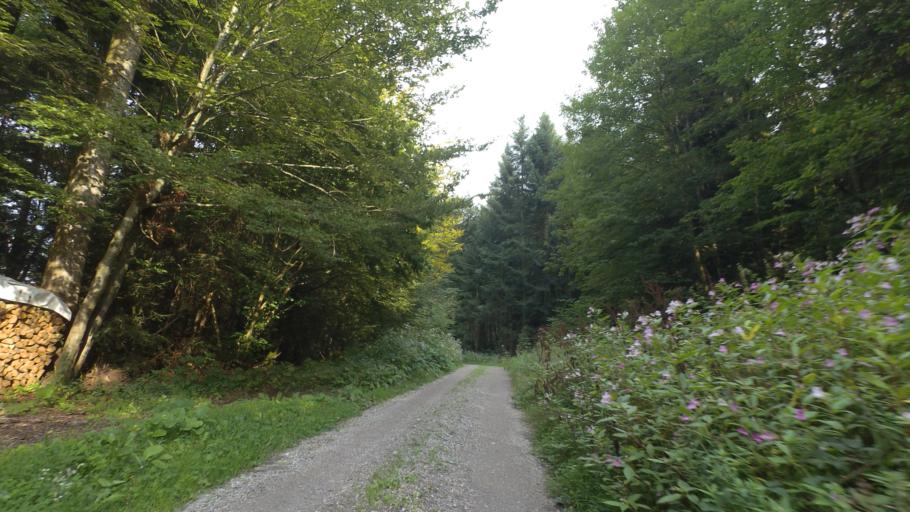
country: DE
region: Bavaria
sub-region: Upper Bavaria
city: Chieming
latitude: 47.9242
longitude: 12.5556
